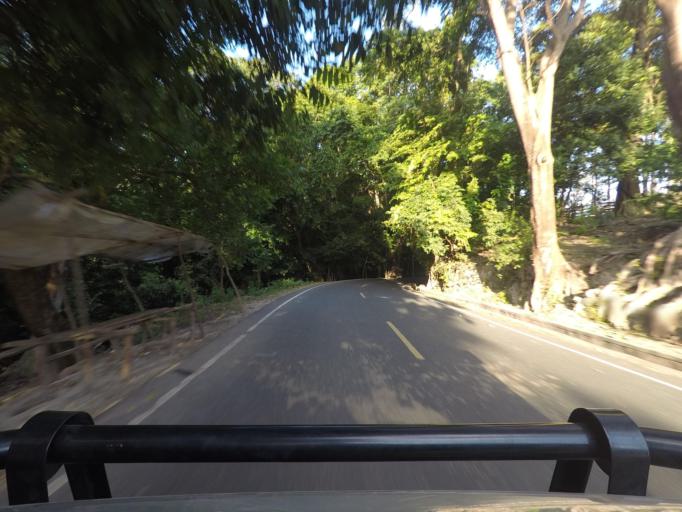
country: TL
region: Bobonaro
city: Maliana
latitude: -8.9522
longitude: 125.0715
